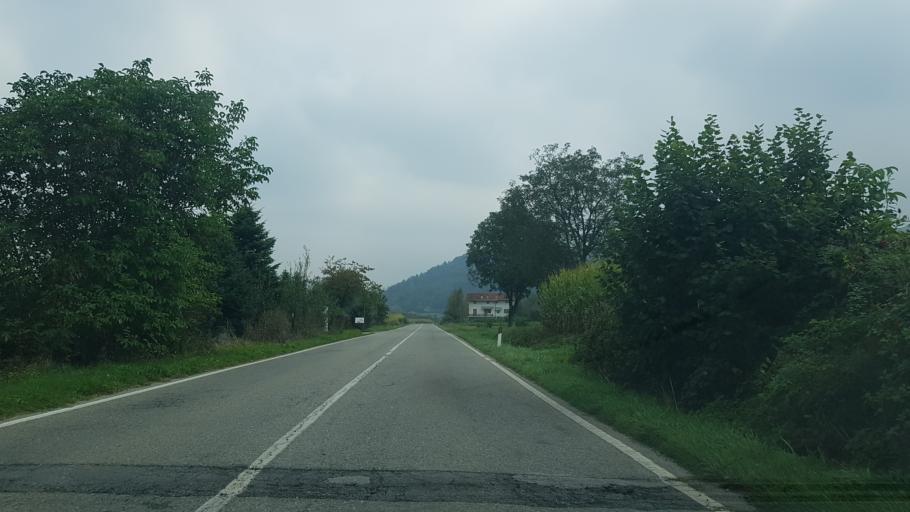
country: IT
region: Piedmont
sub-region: Provincia di Cuneo
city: Peveragno
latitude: 44.3302
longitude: 7.6321
